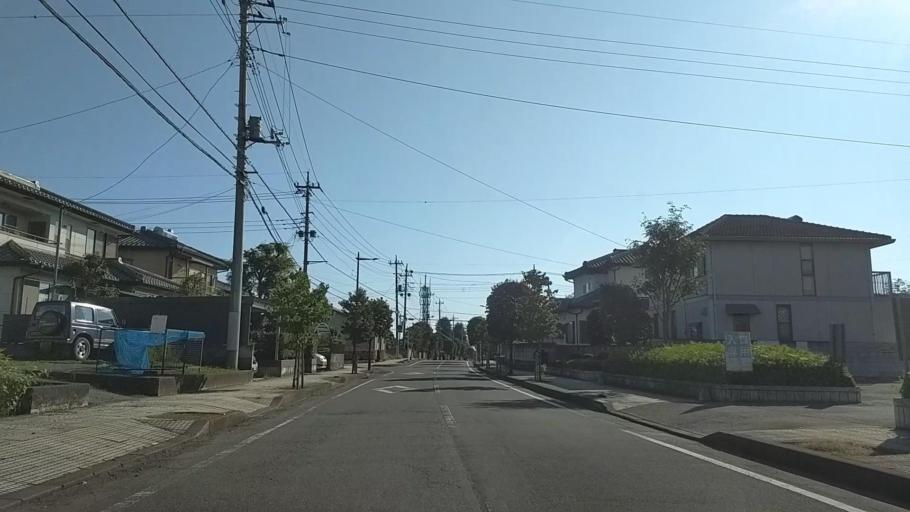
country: JP
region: Gunma
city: Annaka
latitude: 36.3274
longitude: 138.8916
